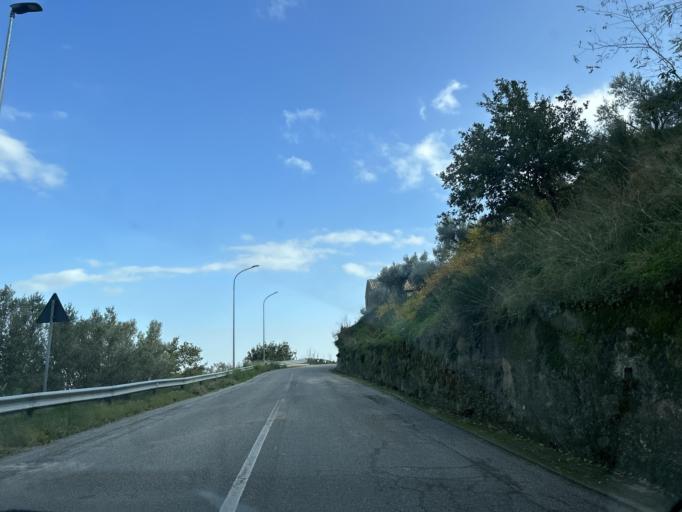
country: IT
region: Calabria
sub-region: Provincia di Catanzaro
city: Montepaone
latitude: 38.7212
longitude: 16.5042
